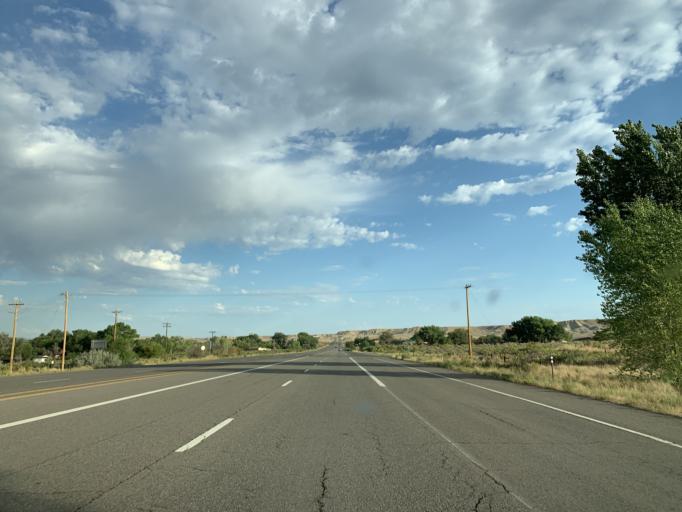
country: US
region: Colorado
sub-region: Mesa County
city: Clifton
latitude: 38.9862
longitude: -108.4455
